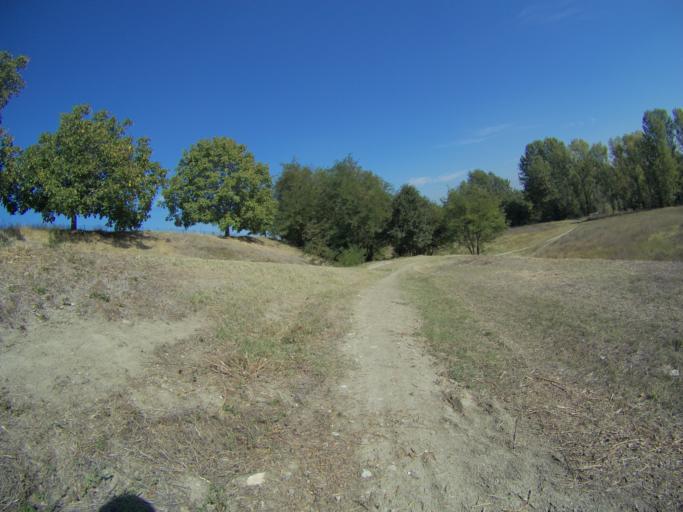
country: IT
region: Emilia-Romagna
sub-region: Provincia di Reggio Emilia
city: Forche
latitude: 44.6439
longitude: 10.5870
